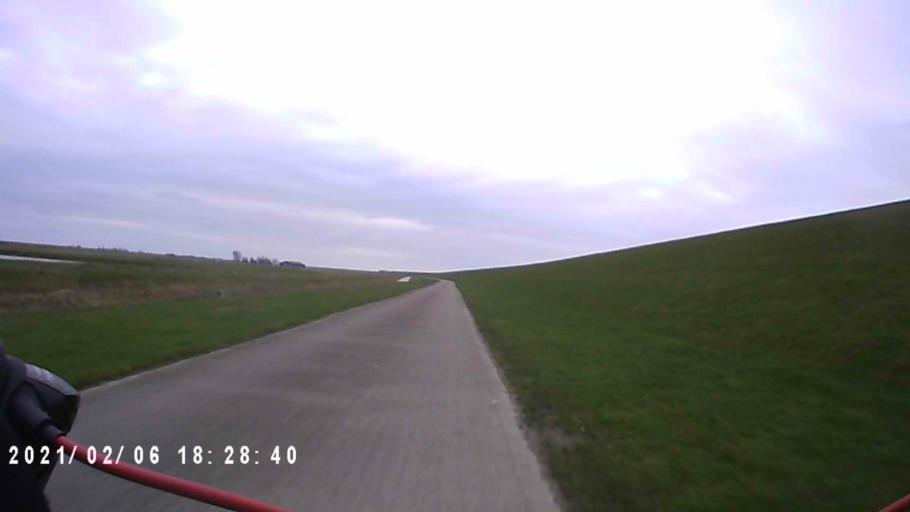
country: DE
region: Lower Saxony
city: Borkum
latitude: 53.4593
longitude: 6.6830
